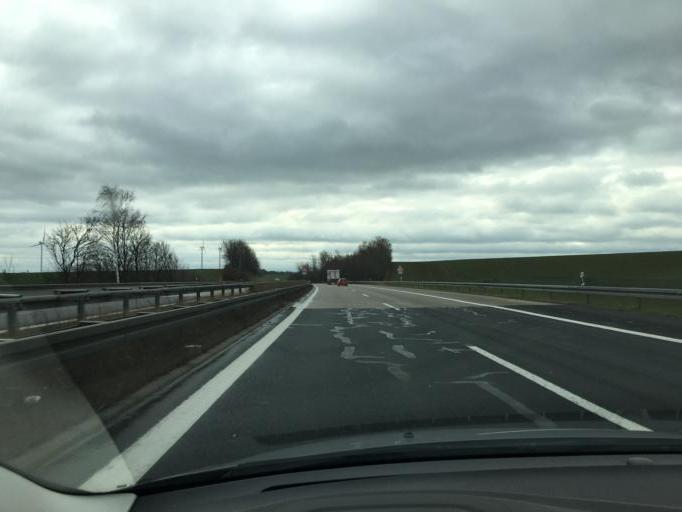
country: DE
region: Saxony
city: Mochau
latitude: 51.1392
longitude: 13.1524
